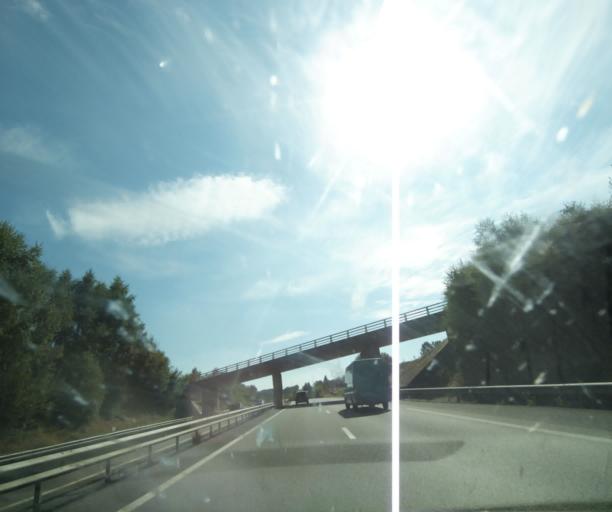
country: FR
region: Limousin
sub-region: Departement de la Correze
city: Sainte-Fereole
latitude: 45.3005
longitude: 1.5734
